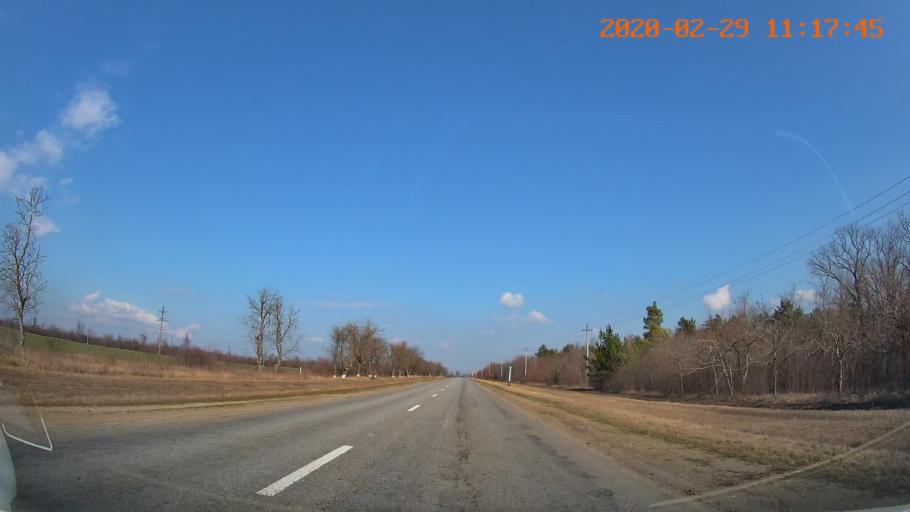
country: MD
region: Telenesti
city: Dubasari
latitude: 47.3258
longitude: 29.1714
